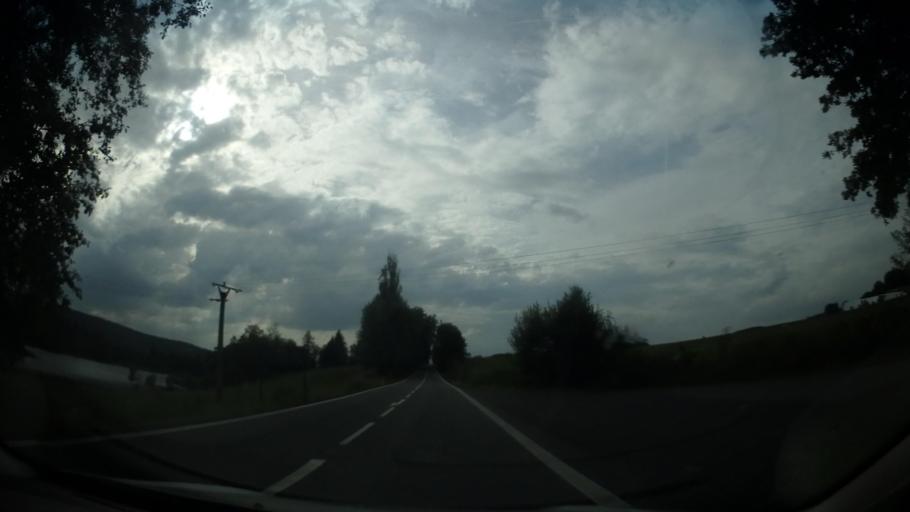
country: CZ
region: Pardubicky
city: Prachovice
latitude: 49.8700
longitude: 15.6226
